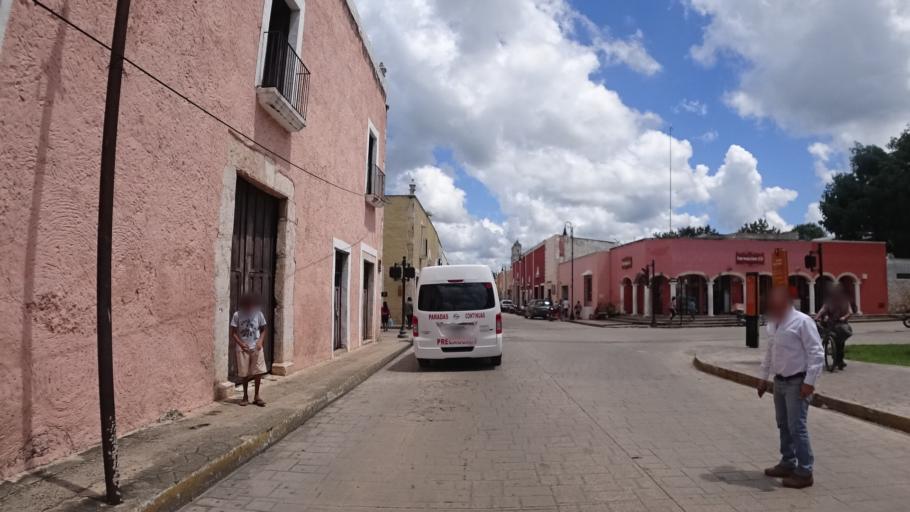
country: MX
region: Yucatan
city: Valladolid
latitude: 20.6897
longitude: -88.2051
